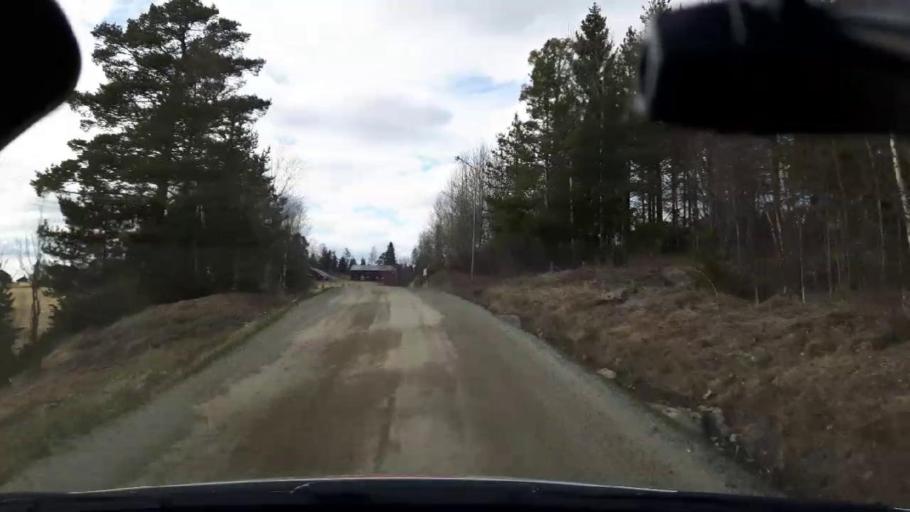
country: SE
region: Jaemtland
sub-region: Bergs Kommun
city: Hoverberg
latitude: 62.8813
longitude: 14.6662
